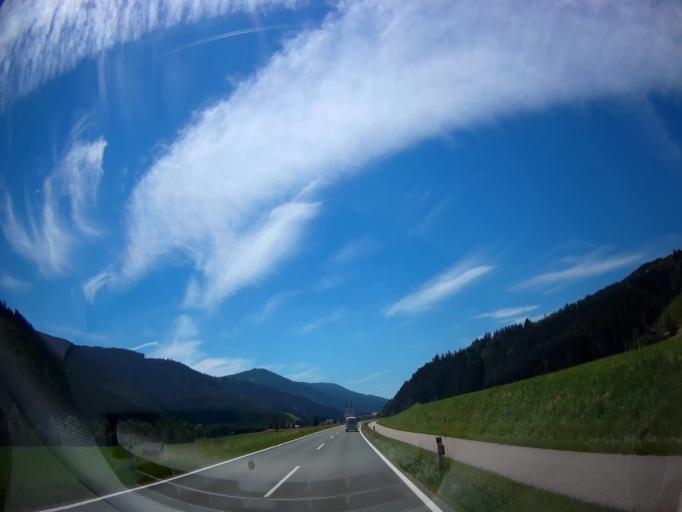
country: AT
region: Carinthia
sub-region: Politischer Bezirk Sankt Veit an der Glan
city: Gurk
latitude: 46.8821
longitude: 14.3074
